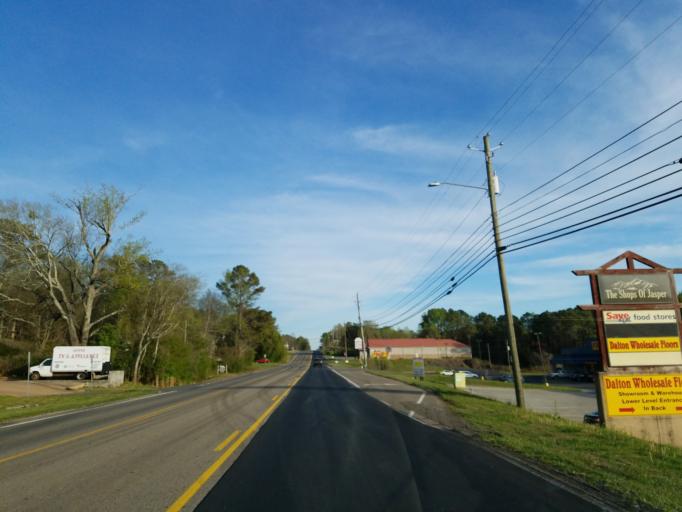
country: US
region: Georgia
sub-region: Pickens County
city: Jasper
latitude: 34.4630
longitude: -84.4164
